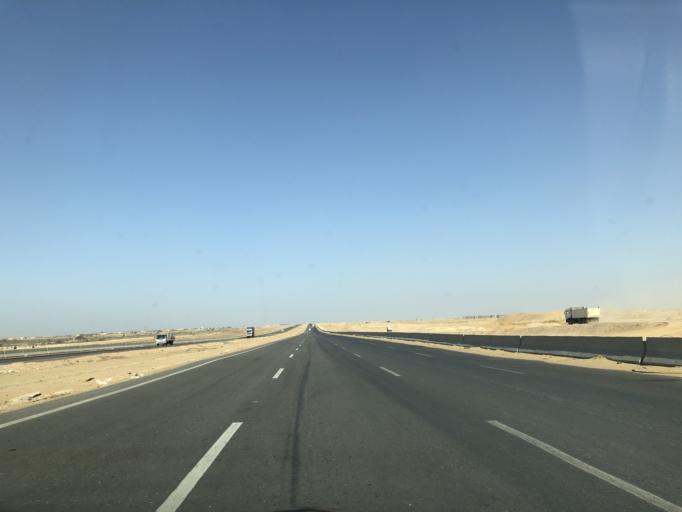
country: EG
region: Muhafazat al Minufiyah
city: Ashmun
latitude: 30.0674
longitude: 30.8524
